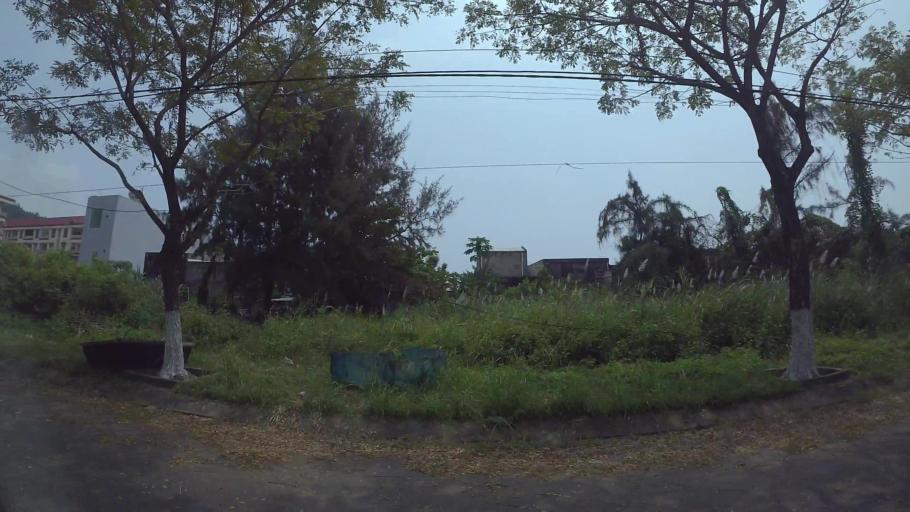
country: VN
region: Da Nang
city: Son Tra
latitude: 16.1054
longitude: 108.2598
